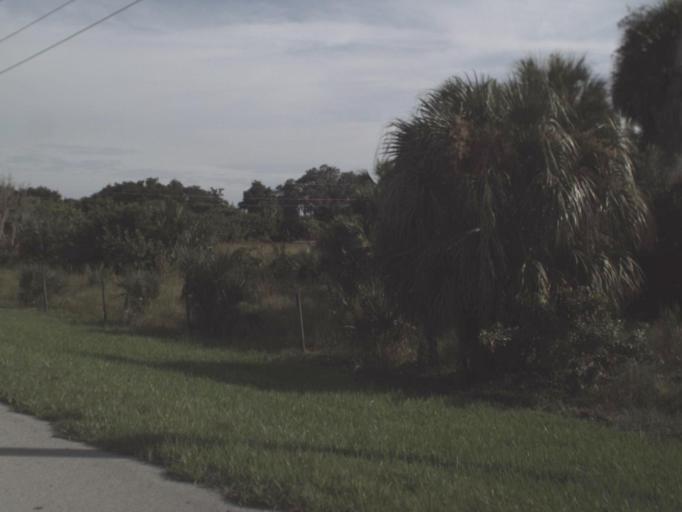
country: US
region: Florida
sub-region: Lee County
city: Fort Myers Shores
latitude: 26.7244
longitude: -81.7609
